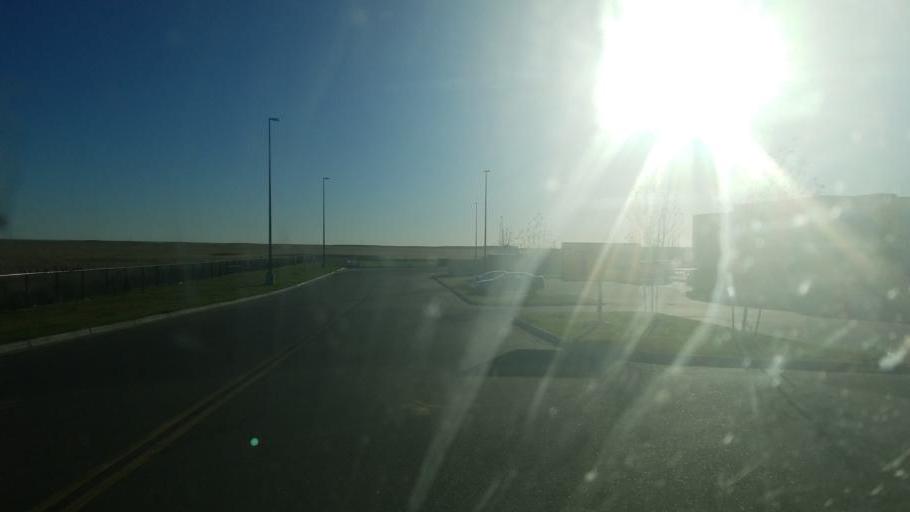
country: US
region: Colorado
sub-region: Kiowa County
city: Eads
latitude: 38.4890
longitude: -102.7853
